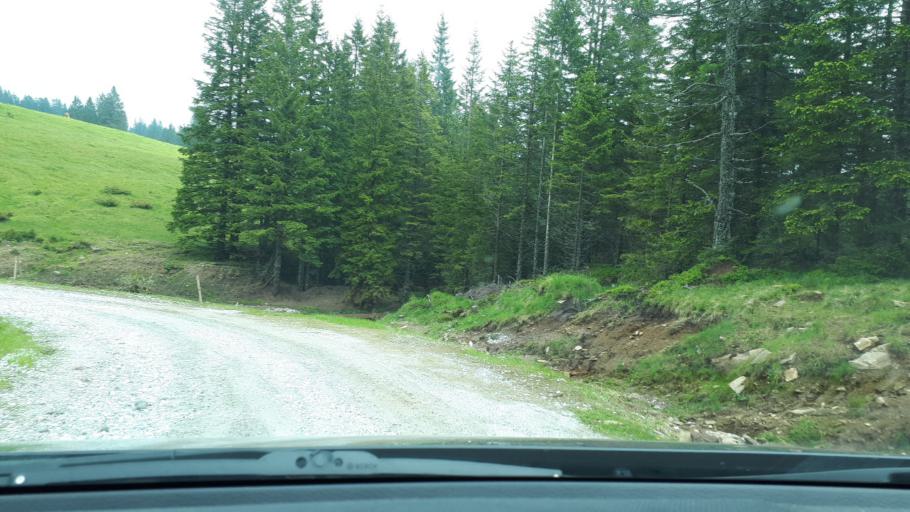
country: AT
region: Styria
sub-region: Politischer Bezirk Voitsberg
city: Modriach
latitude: 46.9116
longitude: 15.0499
